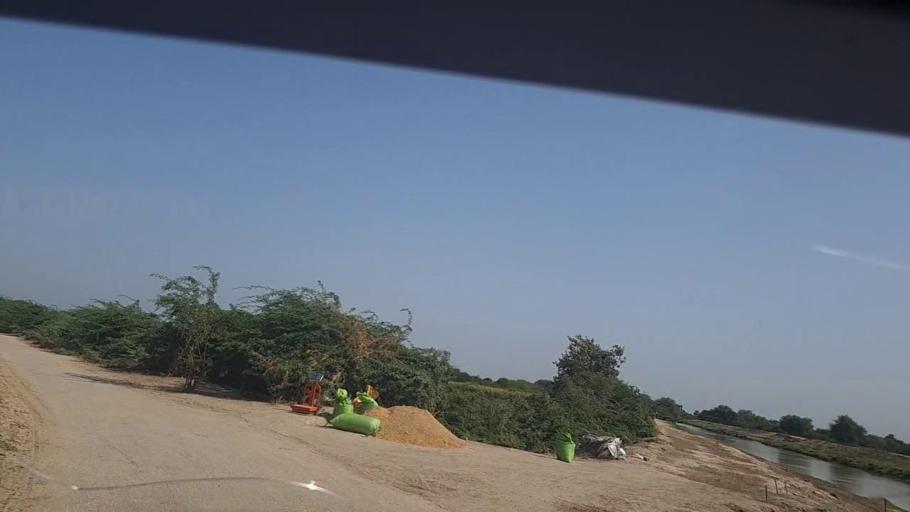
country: PK
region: Sindh
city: Rajo Khanani
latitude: 24.9700
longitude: 68.8719
